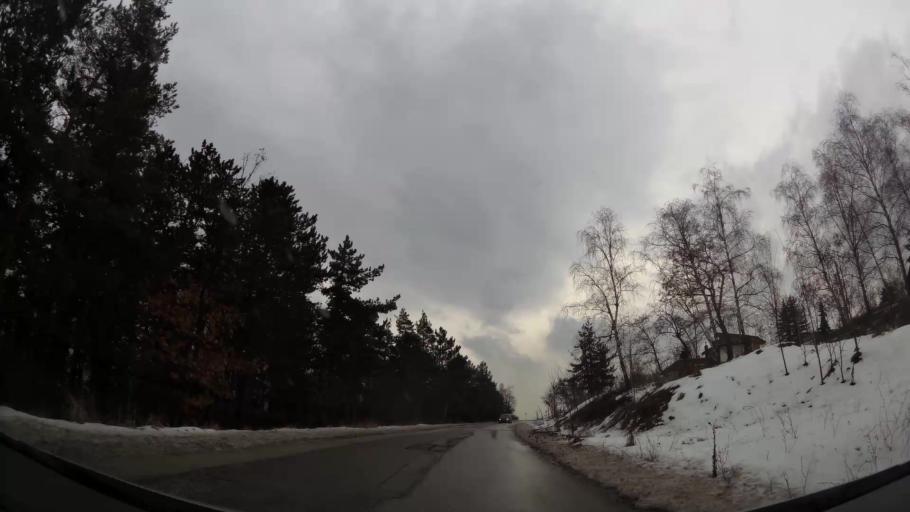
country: BG
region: Sofiya
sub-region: Obshtina Bozhurishte
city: Bozhurishte
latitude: 42.6729
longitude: 23.2213
